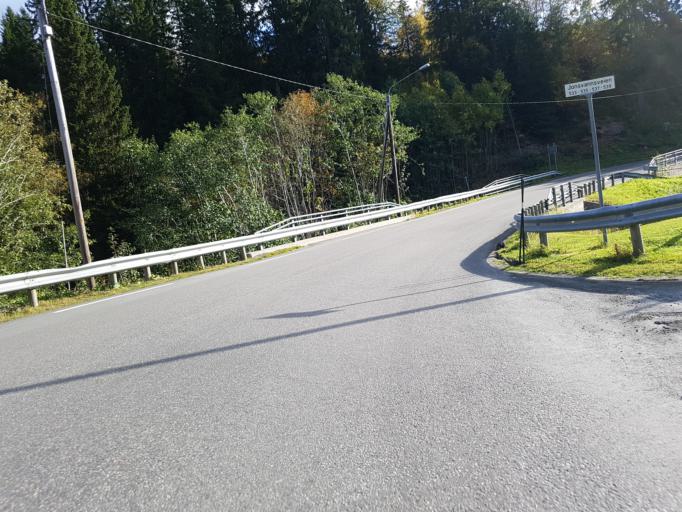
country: NO
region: Sor-Trondelag
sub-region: Klaebu
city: Klaebu
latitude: 63.3996
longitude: 10.5243
